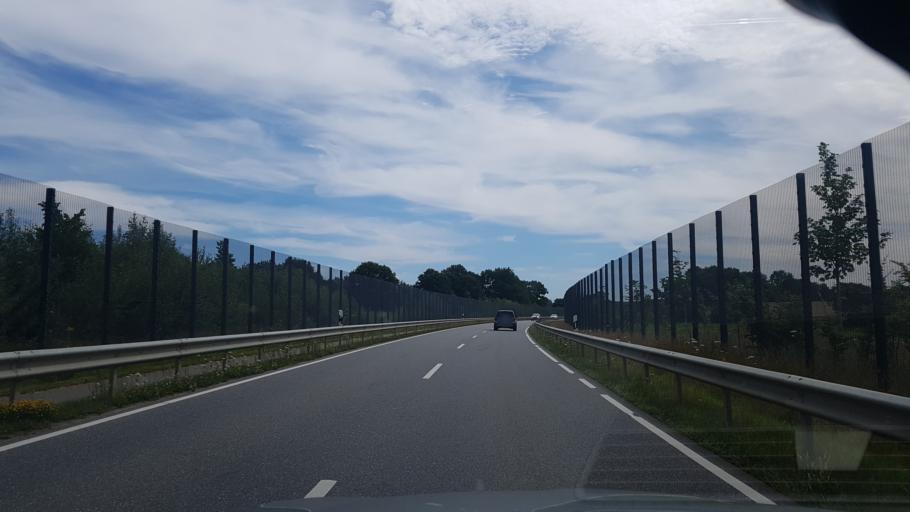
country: DE
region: Schleswig-Holstein
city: Nettelsee
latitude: 54.1708
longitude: 10.1921
